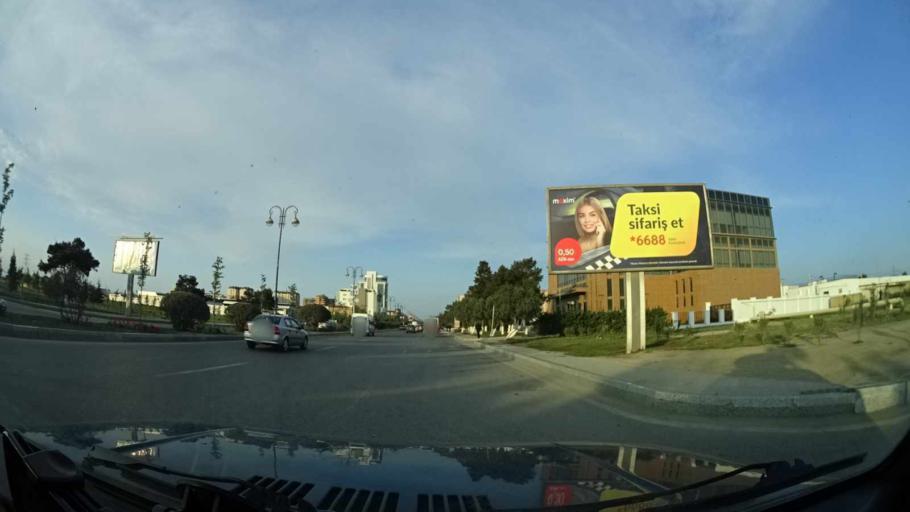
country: AZ
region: Sumqayit
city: Sumqayit
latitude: 40.5832
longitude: 49.6615
